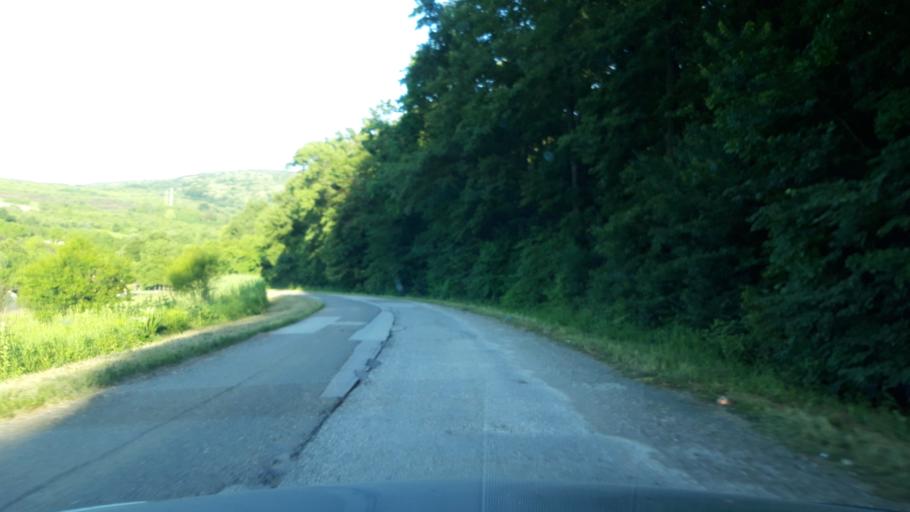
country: RS
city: Glozan
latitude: 45.1592
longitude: 19.5884
